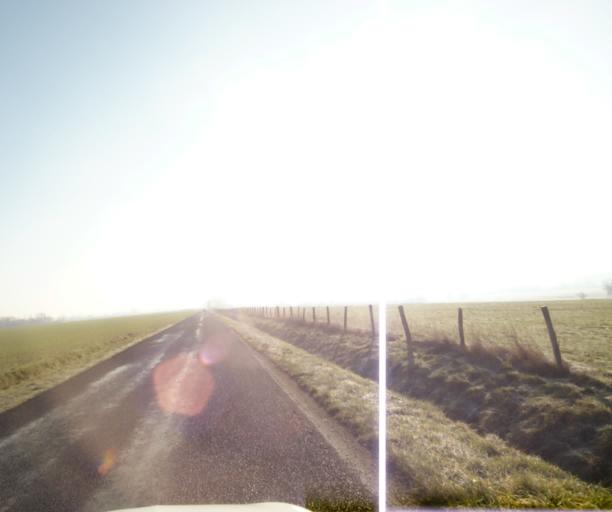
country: FR
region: Champagne-Ardenne
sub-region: Departement de la Haute-Marne
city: Montier-en-Der
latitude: 48.5041
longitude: 4.7358
